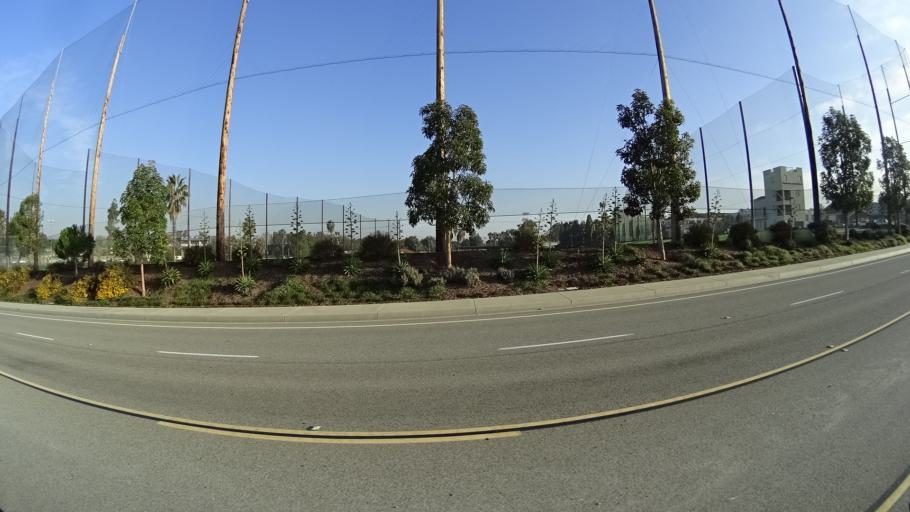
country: US
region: California
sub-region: Orange County
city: Costa Mesa
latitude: 33.6573
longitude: -117.8822
